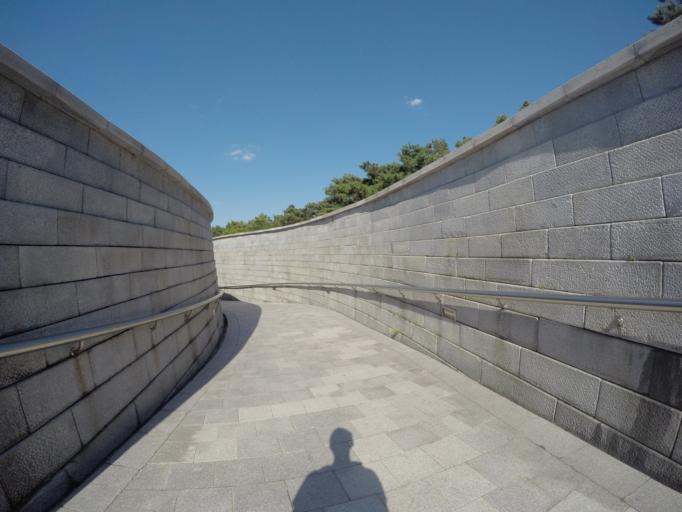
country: KR
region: Seoul
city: Seoul
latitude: 37.5571
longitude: 126.9941
